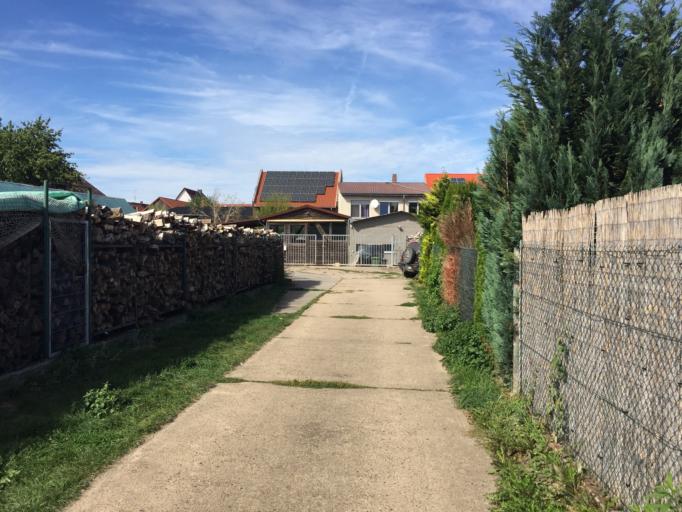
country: DE
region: Hesse
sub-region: Regierungsbezirk Giessen
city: Langgons
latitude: 50.4967
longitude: 8.6627
